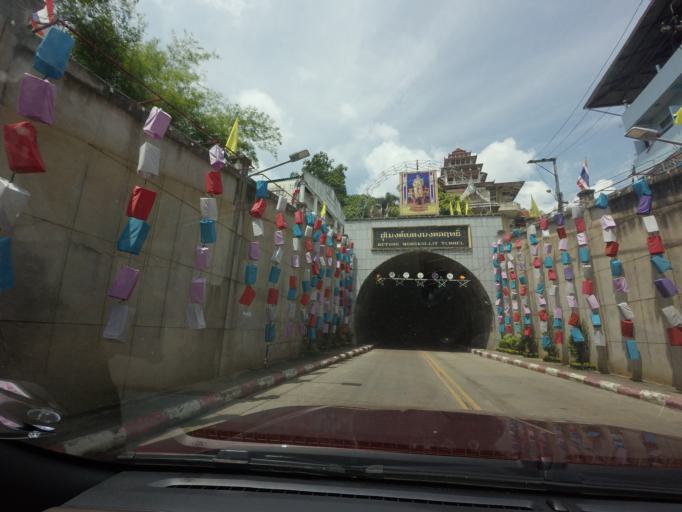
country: TH
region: Yala
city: Betong
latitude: 5.7705
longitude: 101.0715
